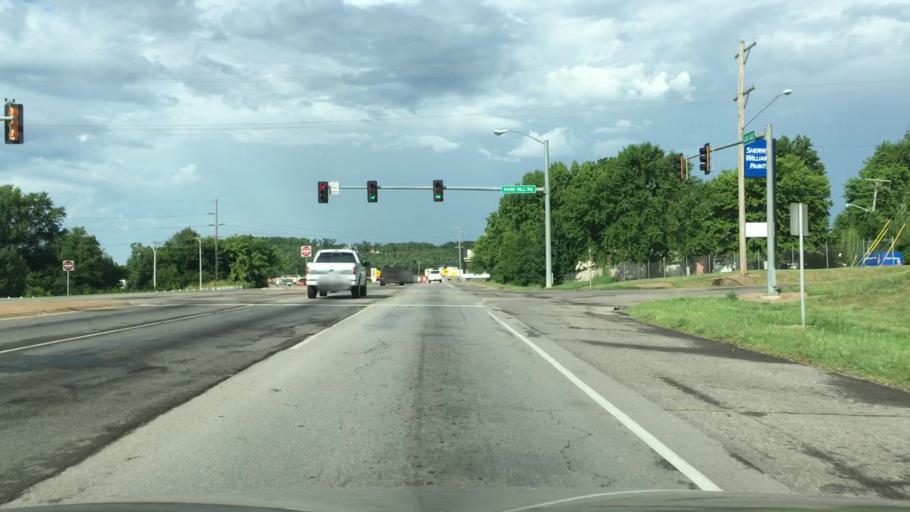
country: US
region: Oklahoma
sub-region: Cherokee County
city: Tahlequah
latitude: 35.8941
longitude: -94.9714
